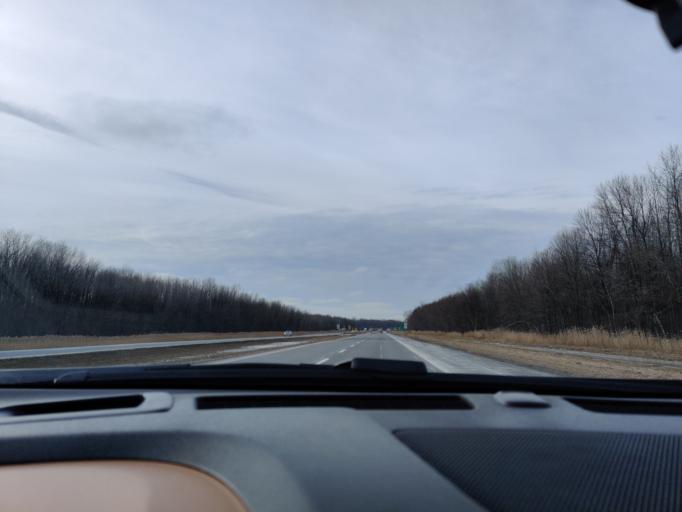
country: CA
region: Quebec
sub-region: Monteregie
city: Les Coteaux
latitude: 45.2311
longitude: -74.2966
